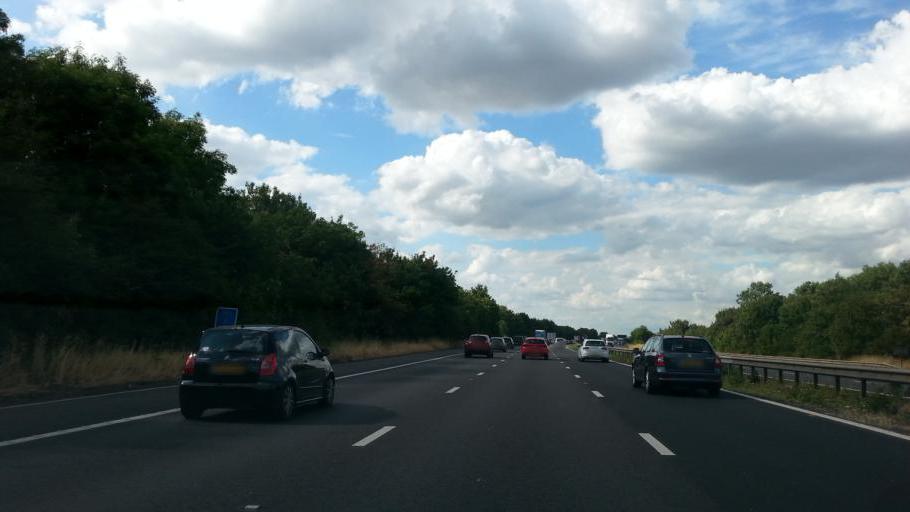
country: GB
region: England
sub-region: Leicestershire
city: Cosby
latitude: 52.5420
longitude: -1.1835
